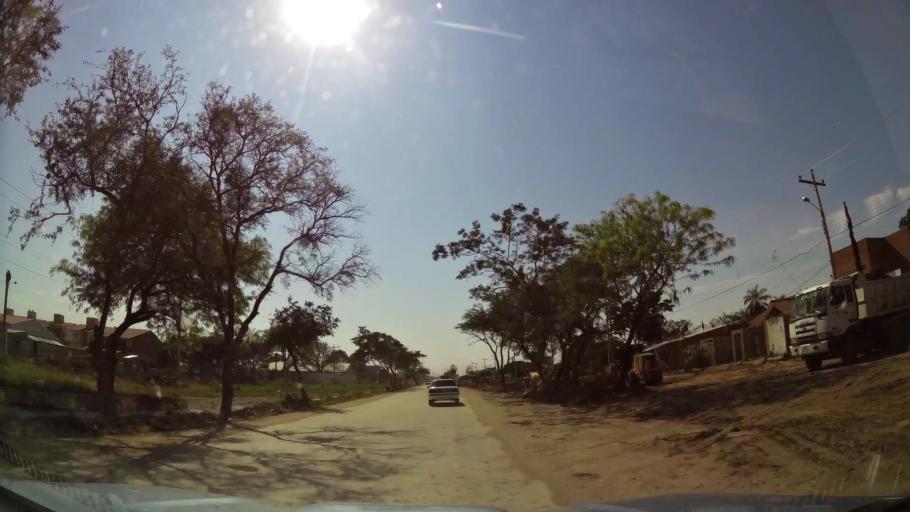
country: BO
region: Santa Cruz
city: Cotoca
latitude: -17.7593
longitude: -63.0913
